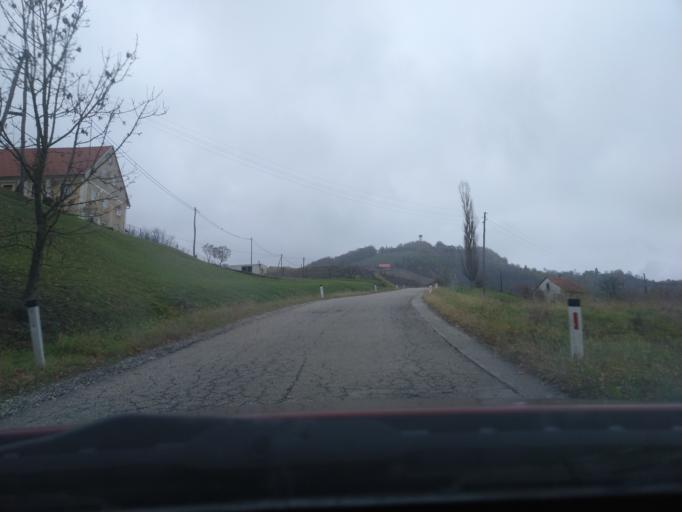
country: SI
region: Kungota
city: Zgornja Kungota
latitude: 46.6724
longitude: 15.6103
